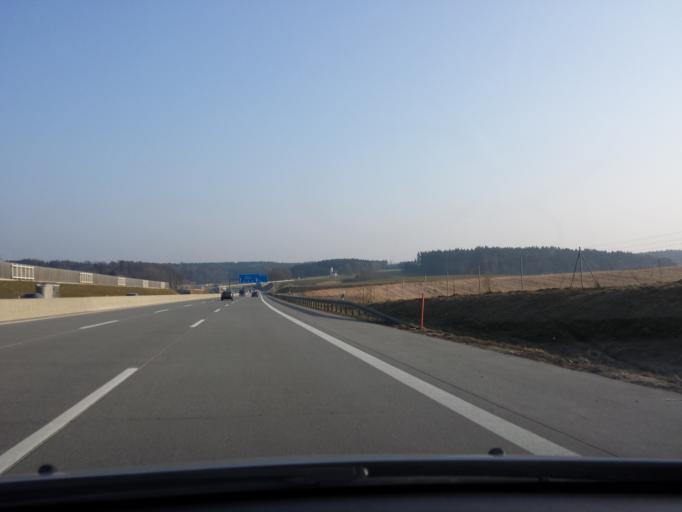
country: DE
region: Bavaria
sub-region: Swabia
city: Adelzhausen
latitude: 48.3584
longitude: 11.1289
